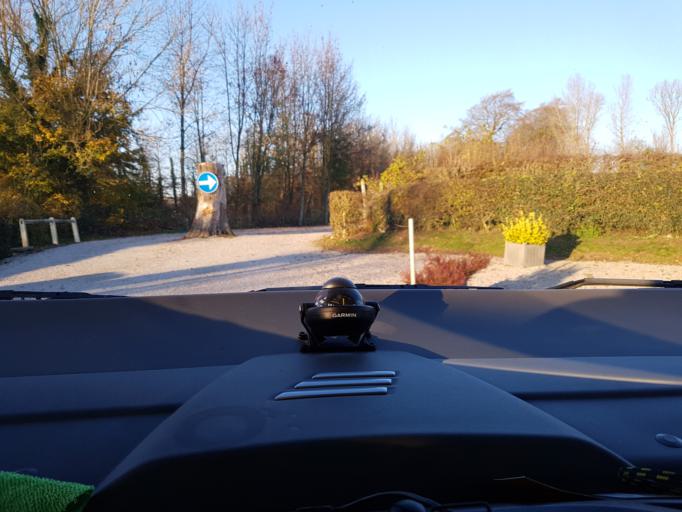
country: FR
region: Nord-Pas-de-Calais
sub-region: Departement du Pas-de-Calais
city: Beaurainville
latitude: 50.4935
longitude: 1.9646
